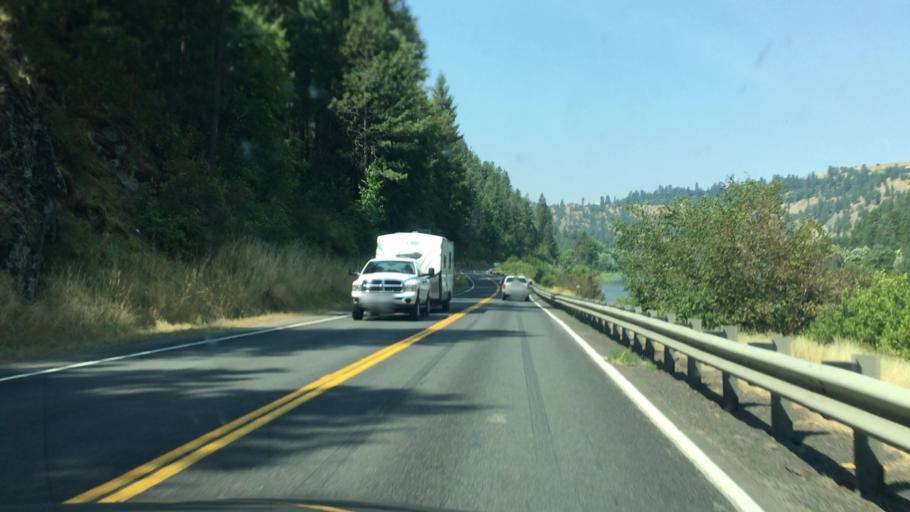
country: US
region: Idaho
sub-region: Clearwater County
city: Orofino
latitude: 46.4971
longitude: -116.4204
